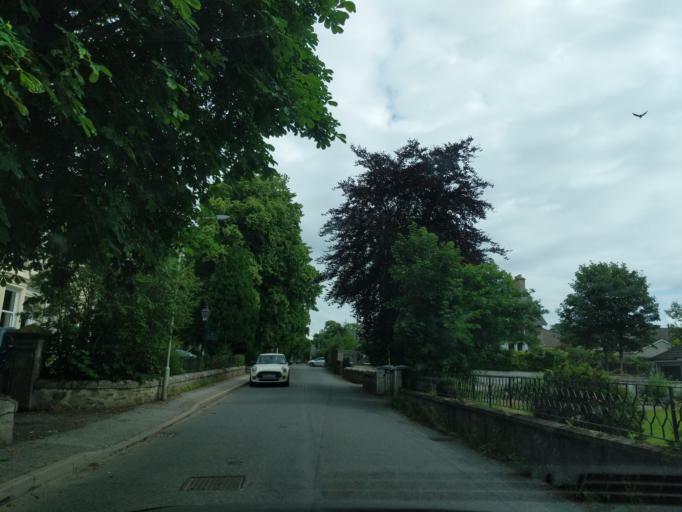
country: GB
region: Scotland
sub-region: Highland
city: Grantown on Spey
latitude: 57.3309
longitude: -3.6111
